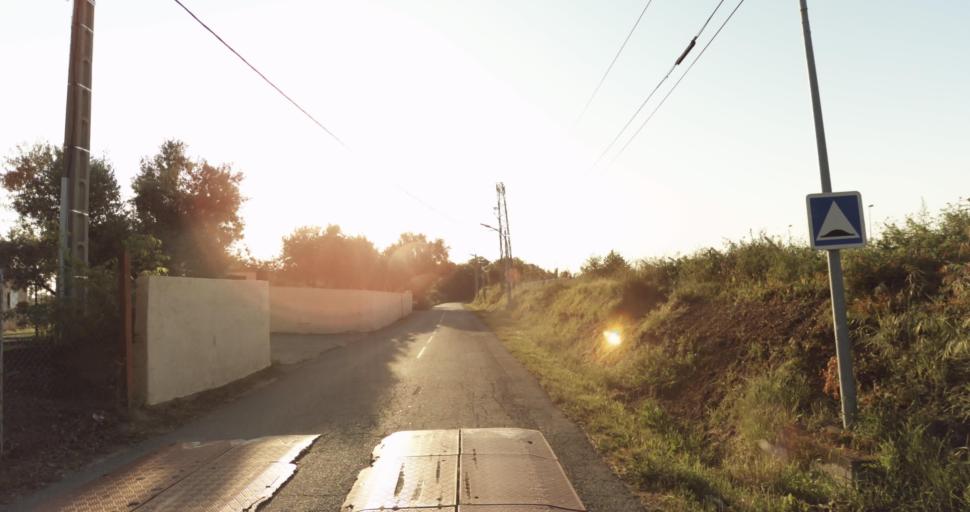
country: FR
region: Corsica
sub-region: Departement de la Haute-Corse
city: Biguglia
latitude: 42.6198
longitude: 9.4390
